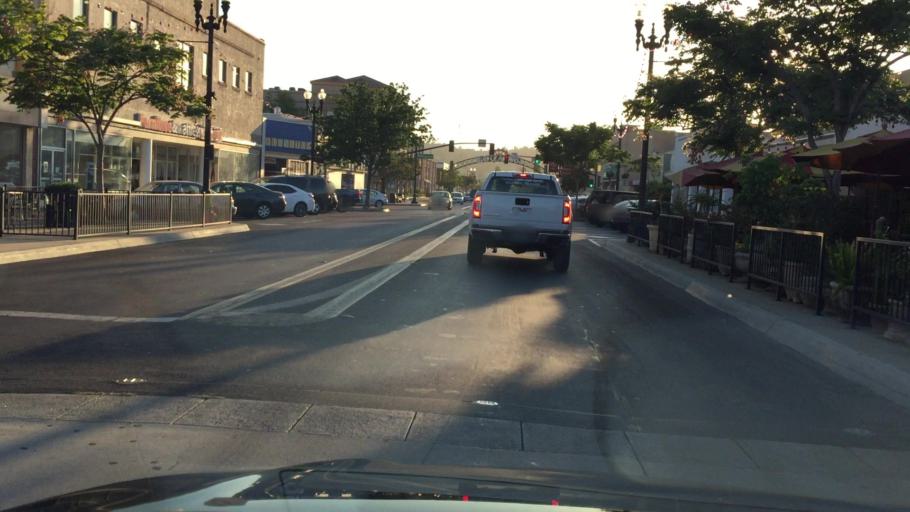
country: US
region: California
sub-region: San Diego County
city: El Cajon
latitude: 32.7950
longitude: -116.9611
